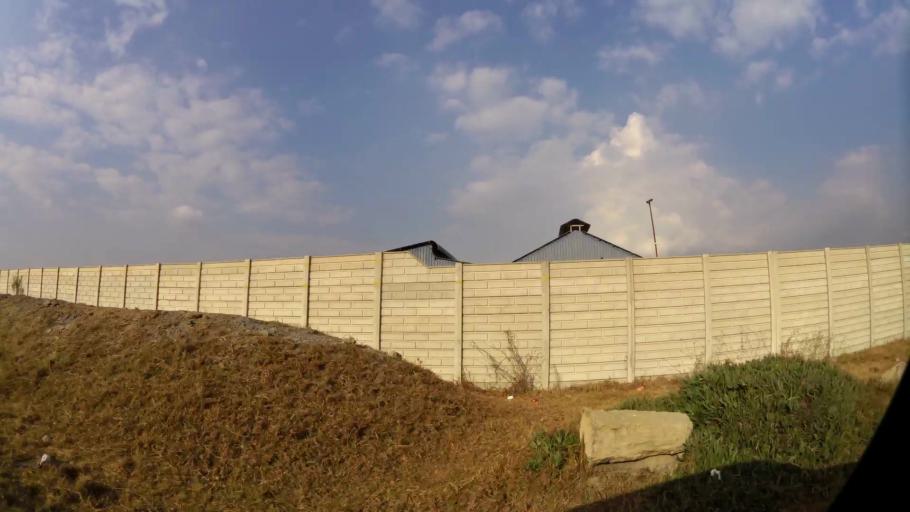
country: ZA
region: Gauteng
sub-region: Sedibeng District Municipality
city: Vereeniging
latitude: -26.6796
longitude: 27.9065
